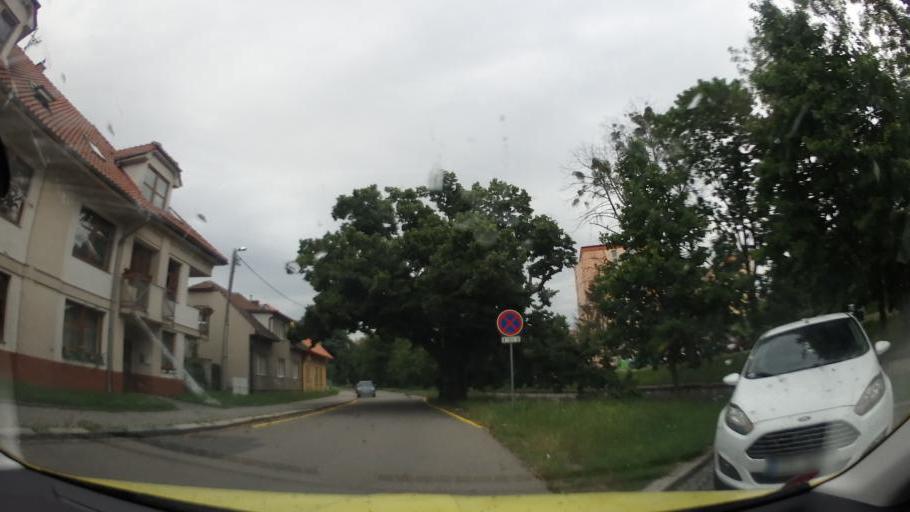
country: CZ
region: Olomoucky
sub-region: Okres Prerov
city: Hranice
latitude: 49.5522
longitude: 17.7334
